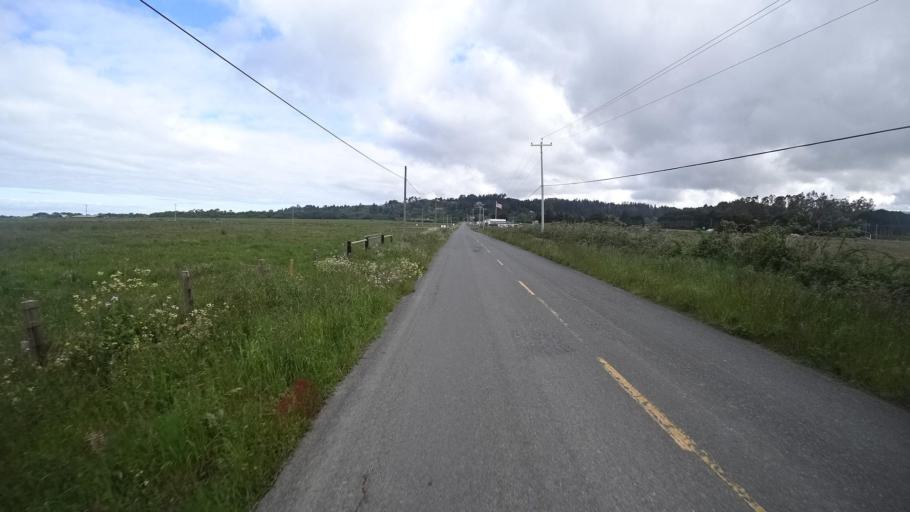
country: US
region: California
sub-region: Humboldt County
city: McKinleyville
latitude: 40.9071
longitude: -124.0914
